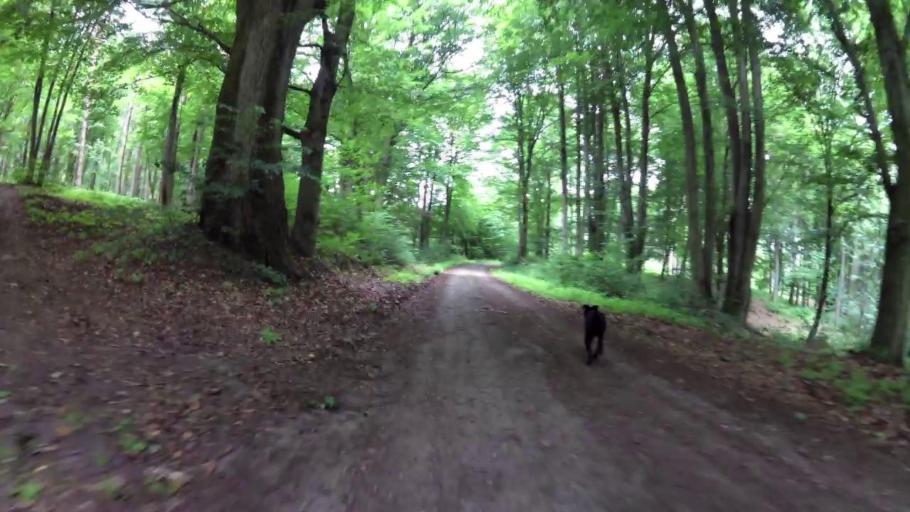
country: PL
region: West Pomeranian Voivodeship
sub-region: Powiat lobeski
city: Lobez
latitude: 53.7525
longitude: 15.6003
